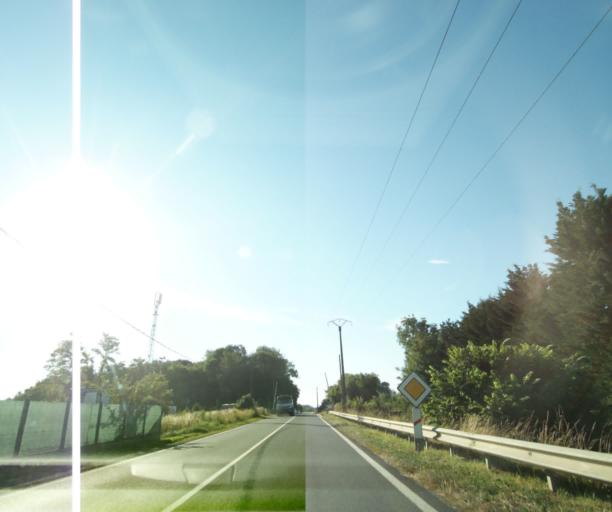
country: FR
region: Ile-de-France
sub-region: Departement de Seine-et-Marne
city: Cannes-Ecluse
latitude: 48.3813
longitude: 2.9766
